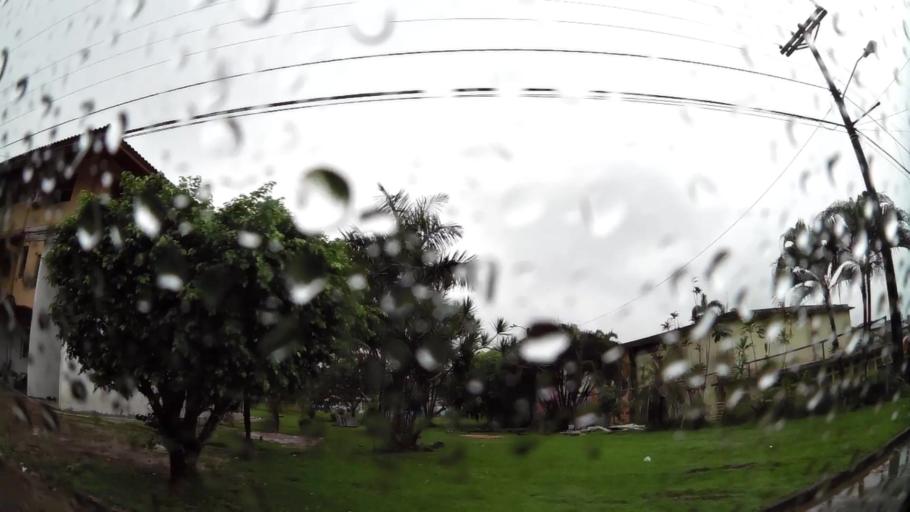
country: PA
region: Colon
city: Las Margaritas
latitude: 9.3123
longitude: -79.8746
